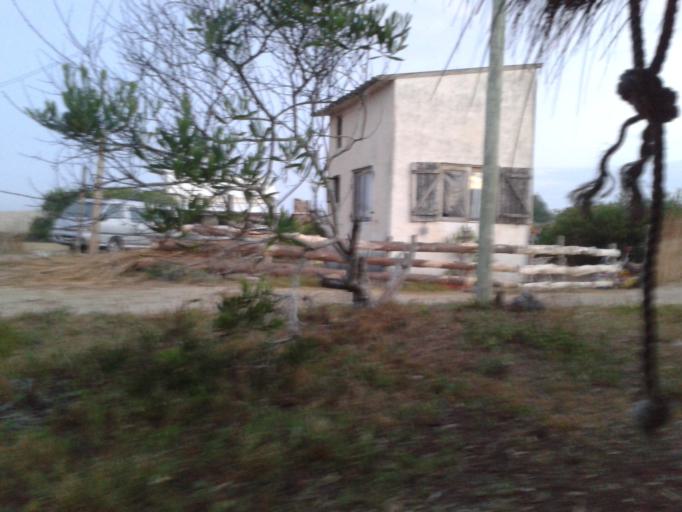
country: UY
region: Rocha
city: Castillos
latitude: -34.3328
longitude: -53.7923
